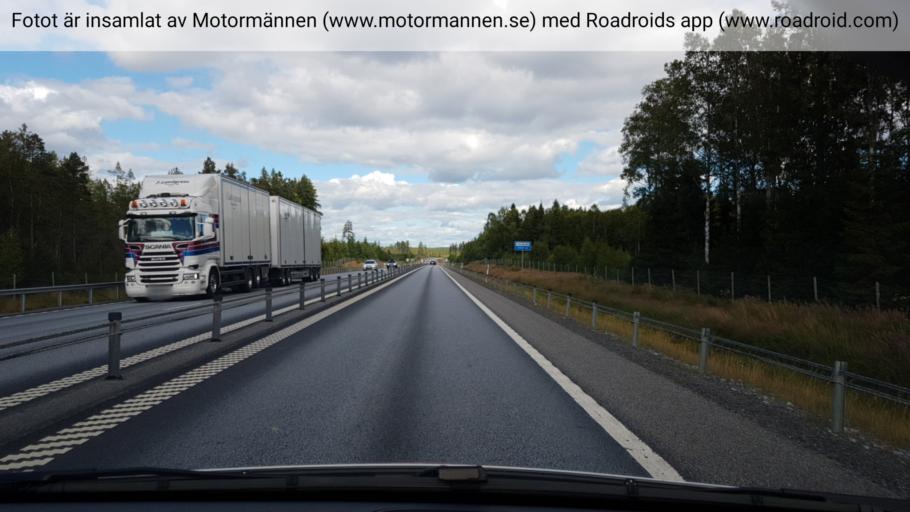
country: SE
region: Vaesterbotten
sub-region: Umea Kommun
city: Hoernefors
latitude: 63.6583
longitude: 19.9586
